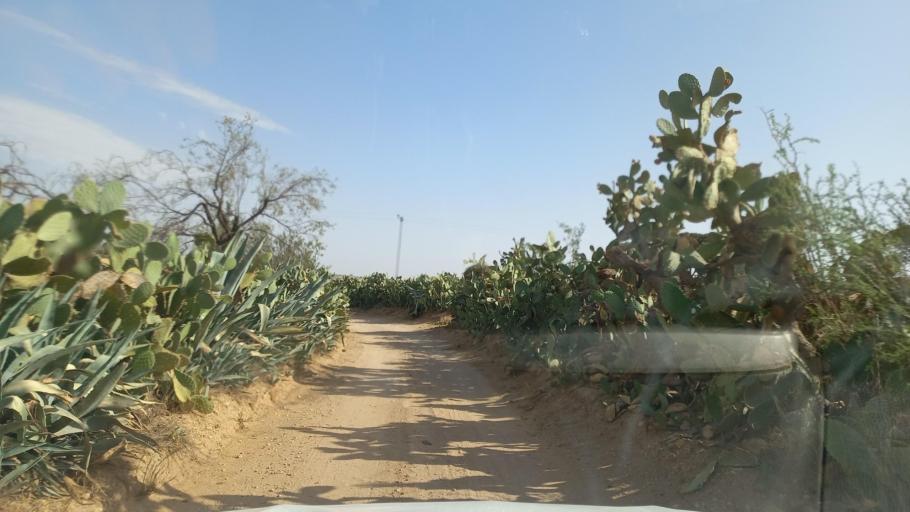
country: TN
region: Al Qasrayn
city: Kasserine
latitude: 35.2524
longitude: 8.9288
